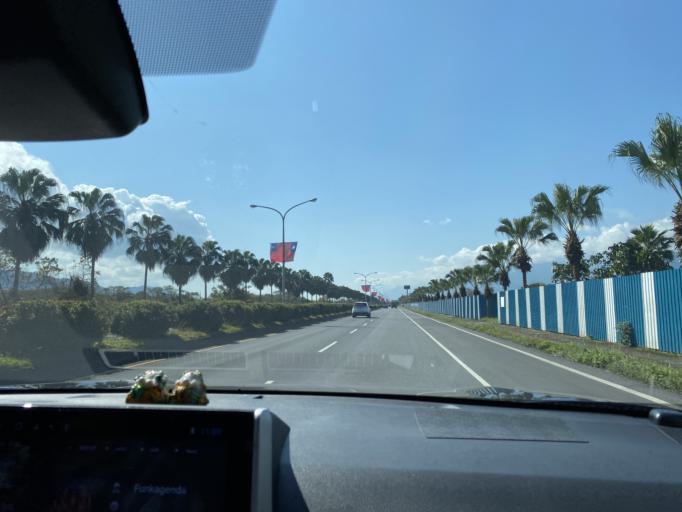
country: TW
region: Taiwan
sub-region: Hualien
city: Hualian
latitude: 23.8689
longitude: 121.5341
